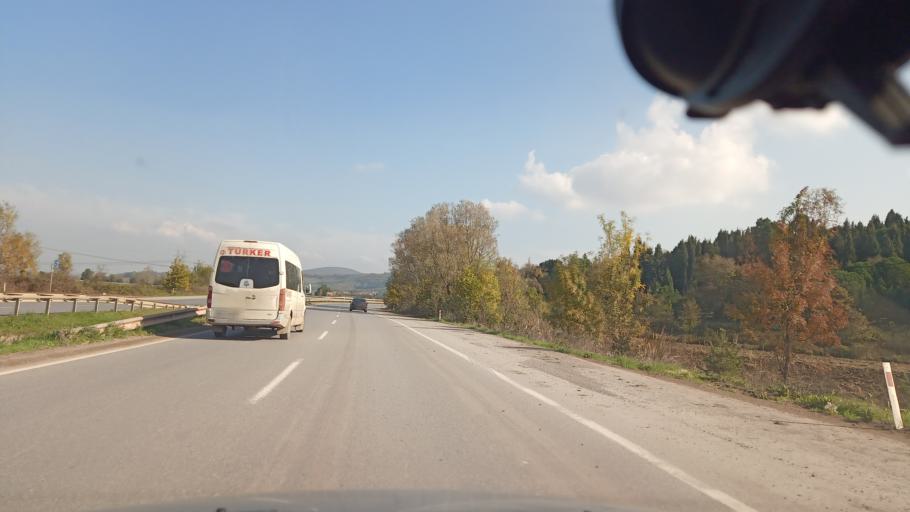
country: TR
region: Sakarya
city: Adapazari
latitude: 40.8285
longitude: 30.3854
